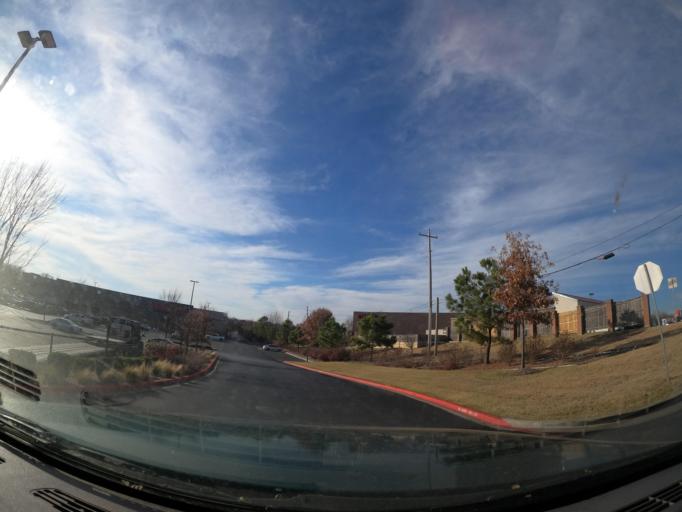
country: US
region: Oklahoma
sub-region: Tulsa County
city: Bixby
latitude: 36.0153
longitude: -95.8874
